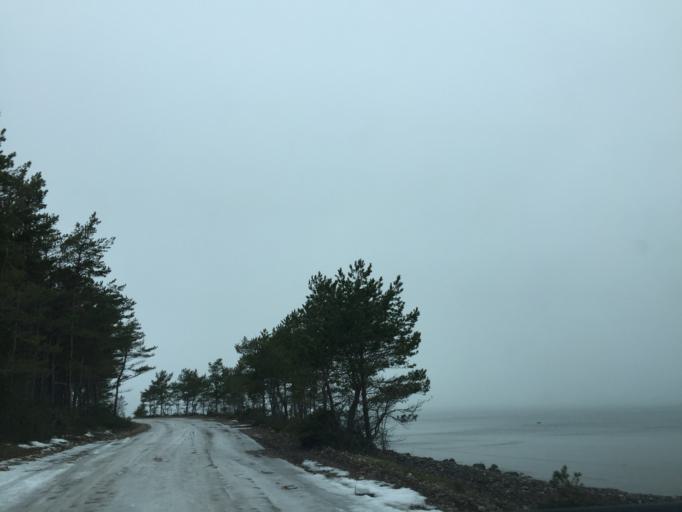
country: EE
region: Saare
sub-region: Kuressaare linn
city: Kuressaare
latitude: 58.5107
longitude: 21.9461
